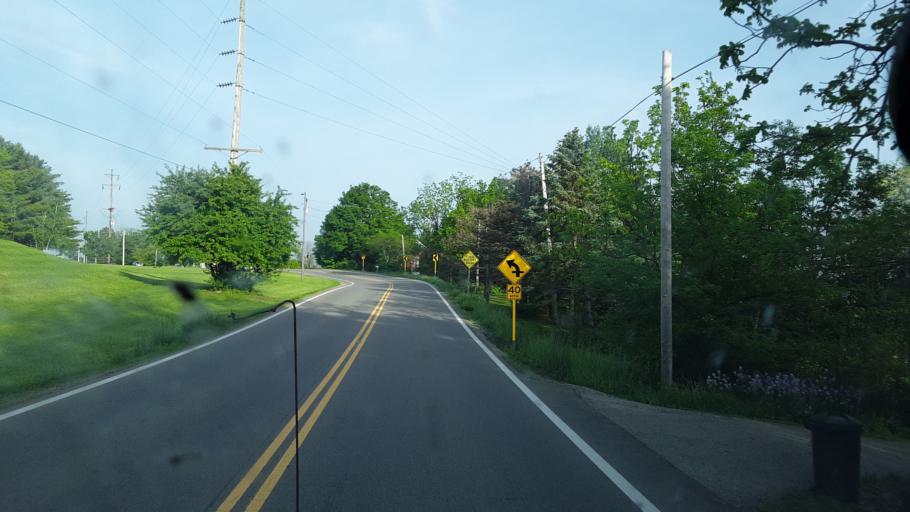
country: US
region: Ohio
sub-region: Ross County
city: Kingston
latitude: 39.5159
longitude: -82.8119
